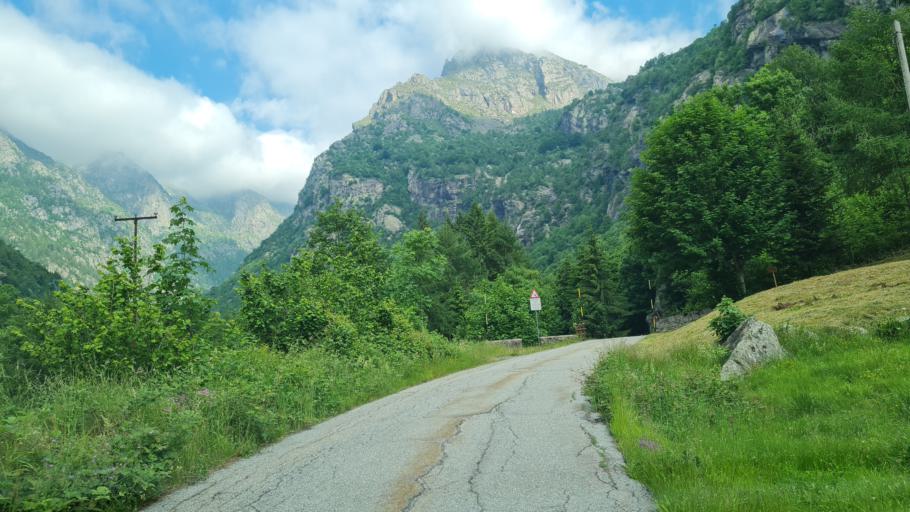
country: IT
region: Piedmont
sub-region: Provincia di Torino
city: Locana
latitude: 45.4514
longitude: 7.4019
